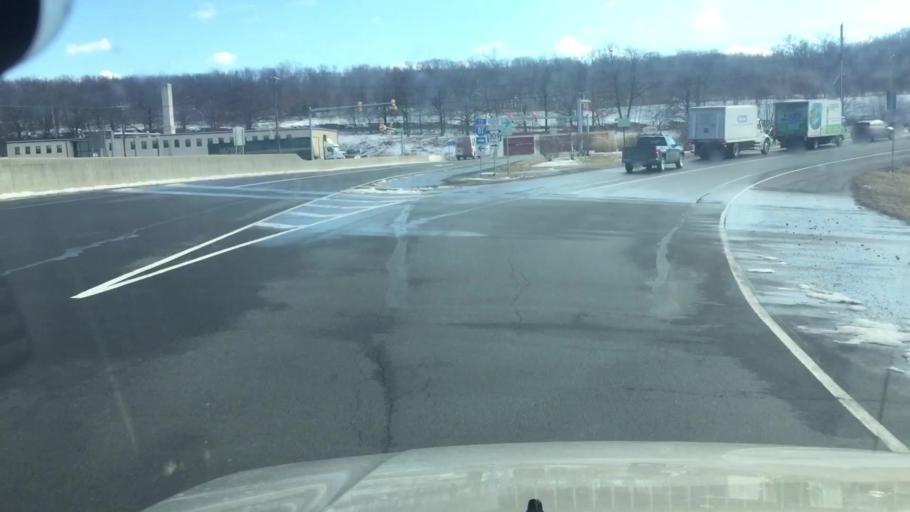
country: US
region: Pennsylvania
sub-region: Luzerne County
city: Hudson
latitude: 41.2528
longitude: -75.8330
